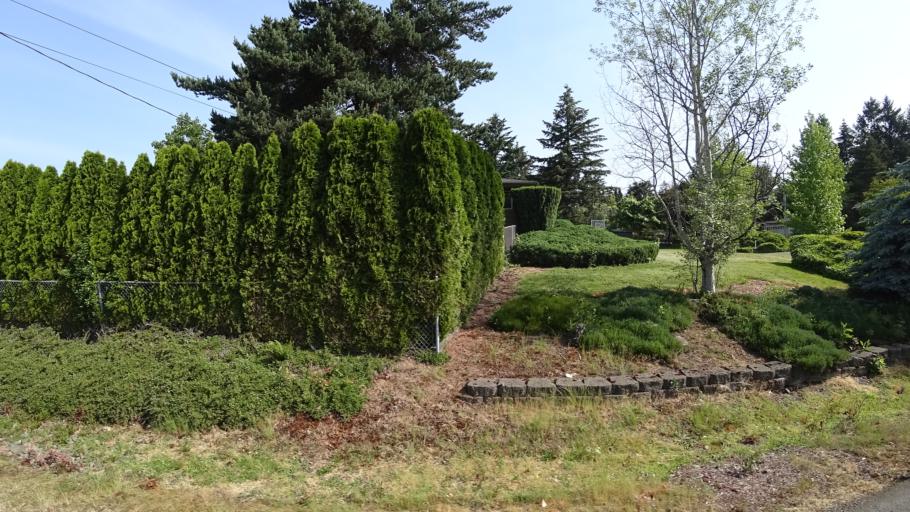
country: US
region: Oregon
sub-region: Clackamas County
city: Happy Valley
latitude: 45.4581
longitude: -122.5227
